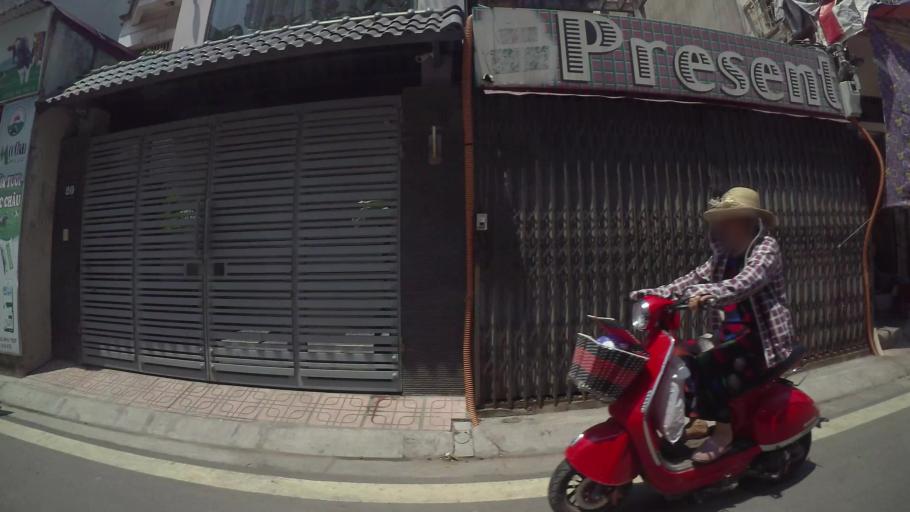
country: VN
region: Ha Noi
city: Hoan Kiem
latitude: 21.0447
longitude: 105.8751
